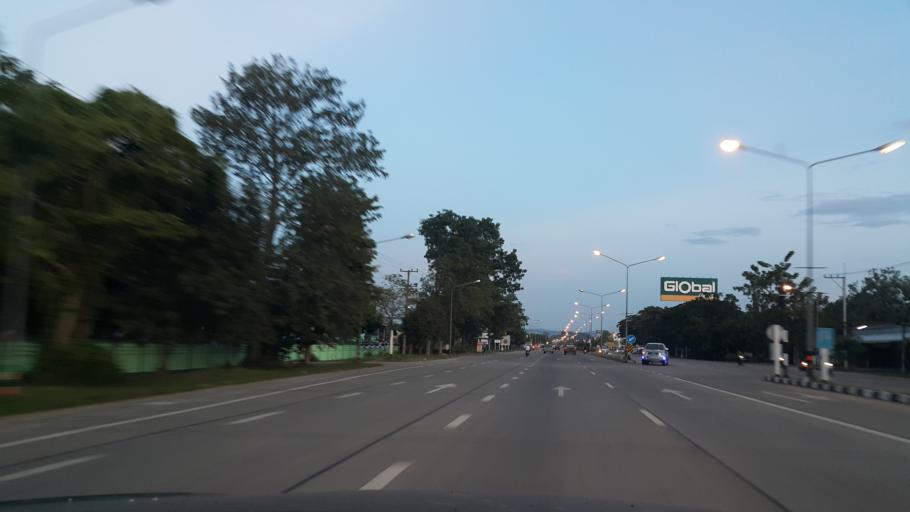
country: TH
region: Lamphun
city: Lamphun
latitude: 18.5636
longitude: 99.0318
